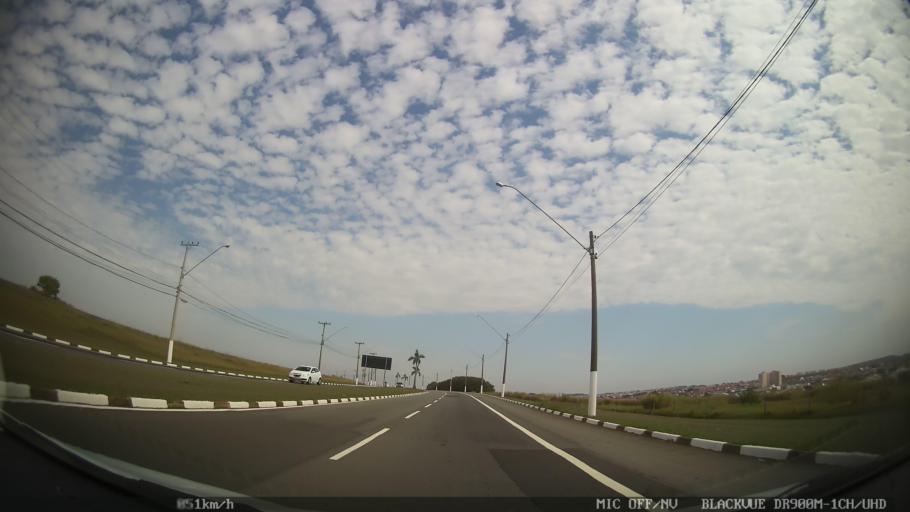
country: BR
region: Sao Paulo
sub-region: Paulinia
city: Paulinia
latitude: -22.7899
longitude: -47.1696
